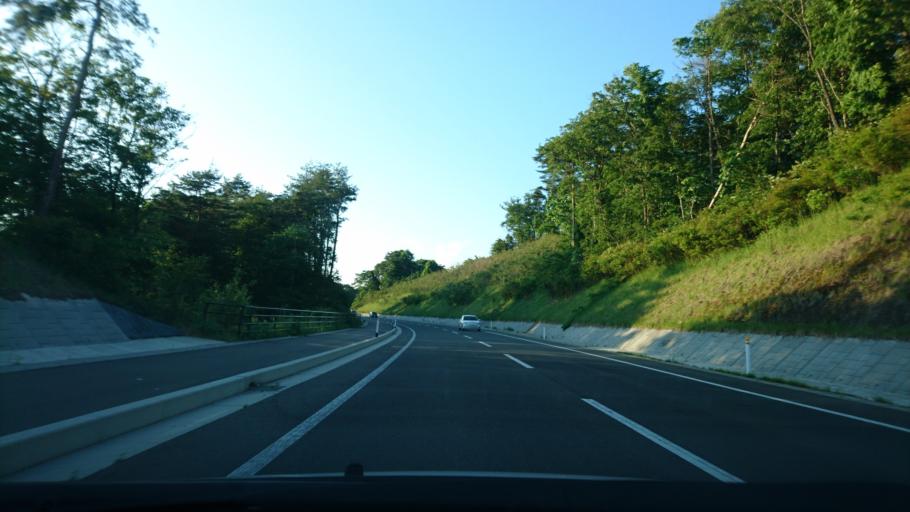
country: JP
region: Iwate
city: Ichinoseki
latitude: 38.8756
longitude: 141.1608
